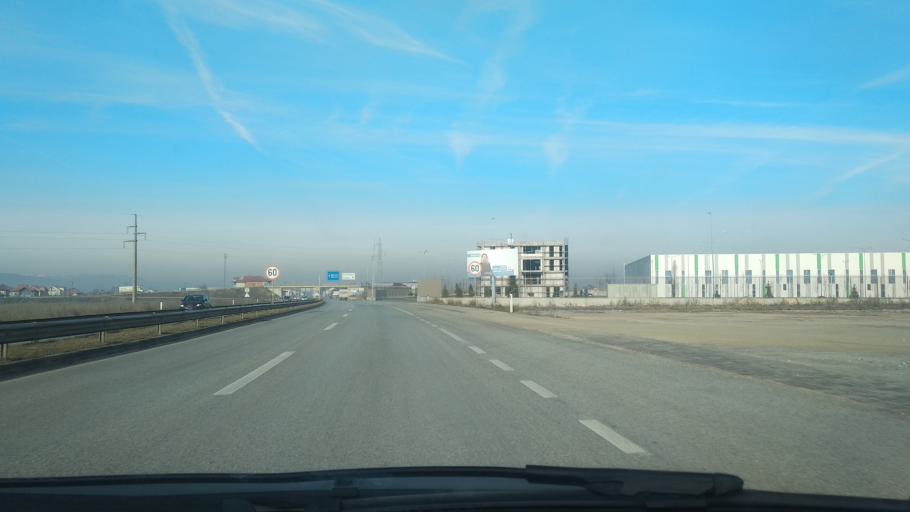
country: XK
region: Pristina
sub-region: Komuna e Obiliqit
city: Obiliq
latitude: 42.7156
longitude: 21.0963
